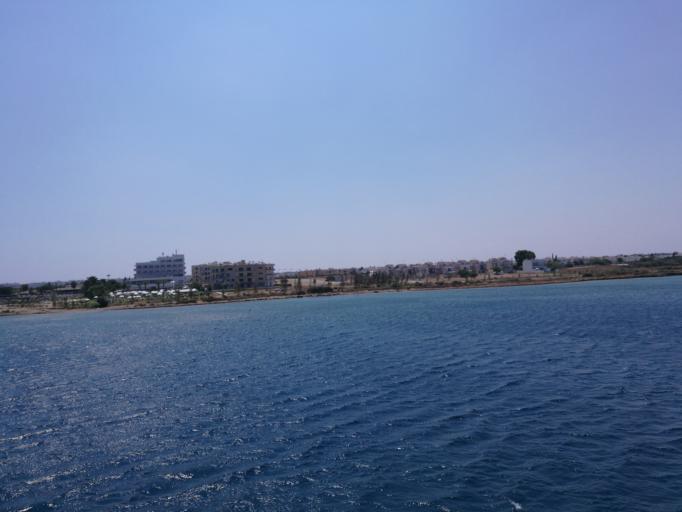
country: CY
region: Ammochostos
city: Protaras
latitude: 35.0471
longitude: 34.0332
